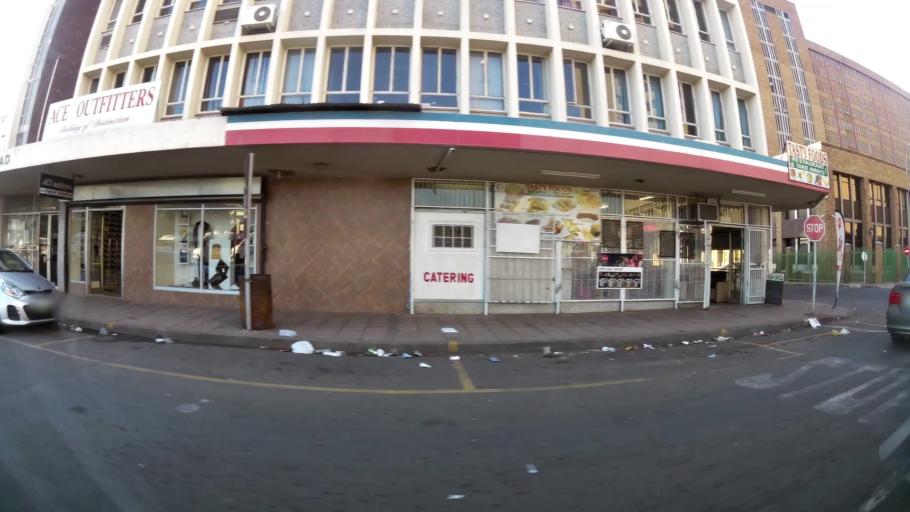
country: ZA
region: Northern Cape
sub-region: Frances Baard District Municipality
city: Kimberley
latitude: -28.7374
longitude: 24.7647
